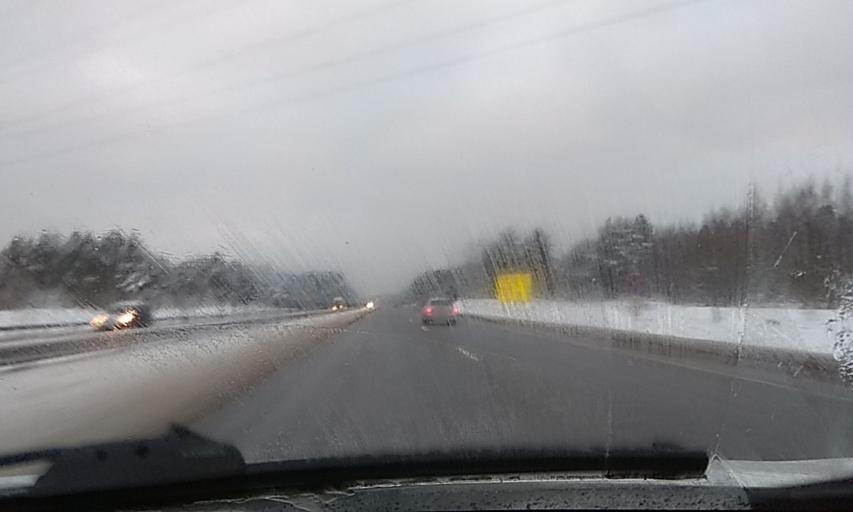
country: LT
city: Grigiskes
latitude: 54.6624
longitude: 25.1295
